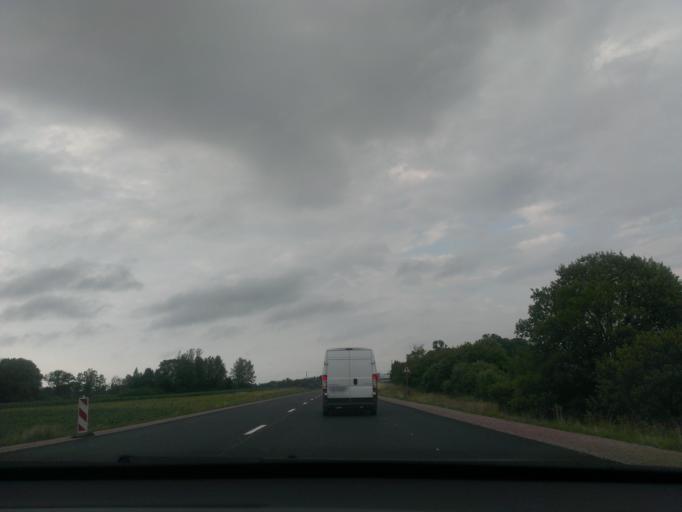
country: LV
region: Lecava
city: Iecava
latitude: 56.6177
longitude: 24.2172
